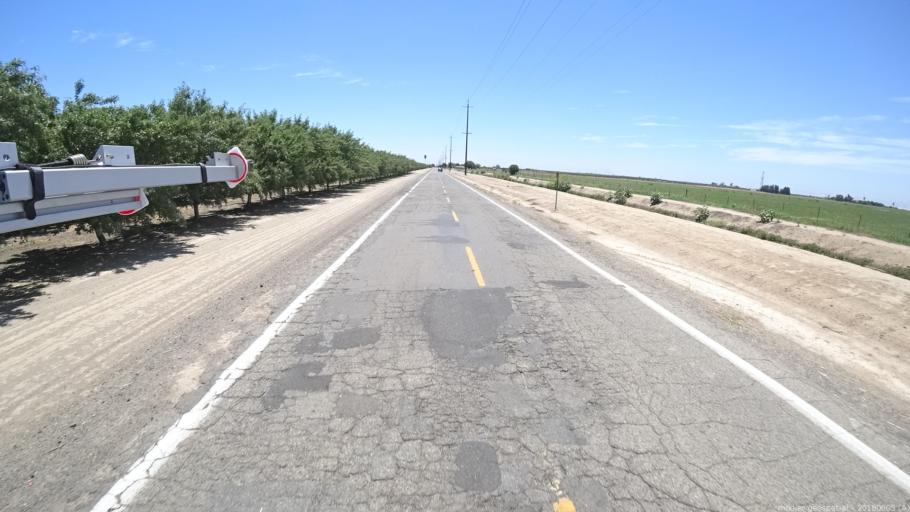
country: US
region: California
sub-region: Madera County
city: Chowchilla
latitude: 37.0954
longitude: -120.3108
